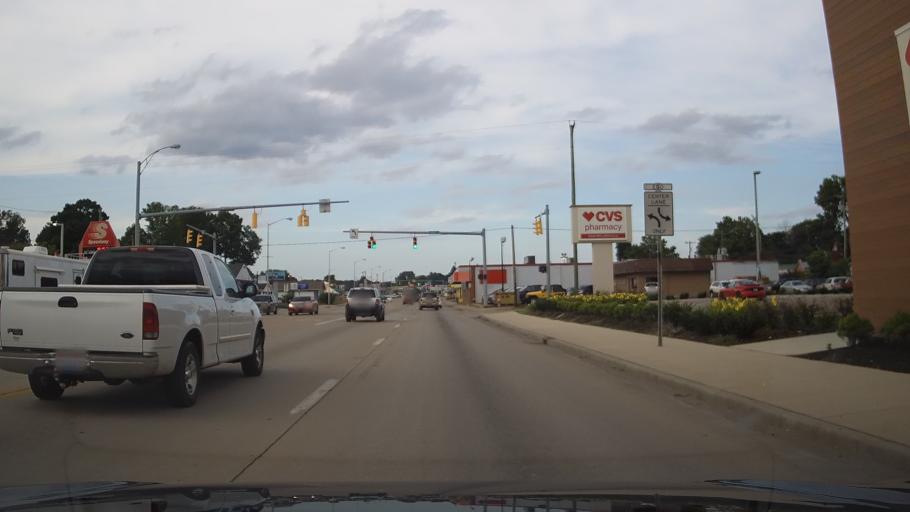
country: US
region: Ohio
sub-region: Pike County
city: Waverly
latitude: 39.1284
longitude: -82.9840
